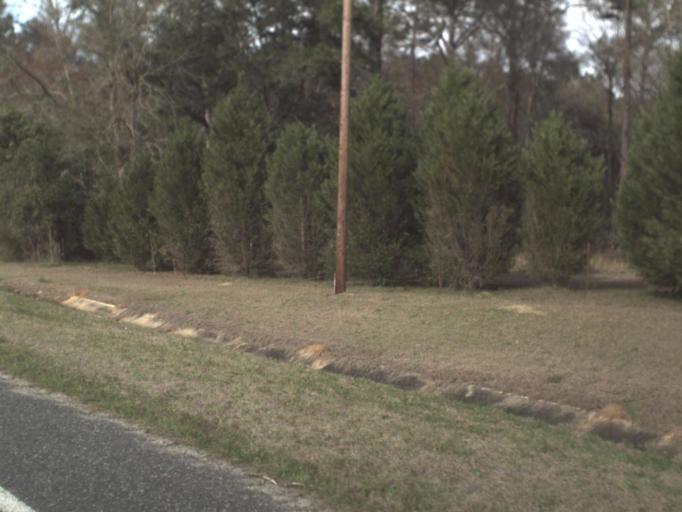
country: US
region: Florida
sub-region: Jefferson County
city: Monticello
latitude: 30.5996
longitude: -83.8712
